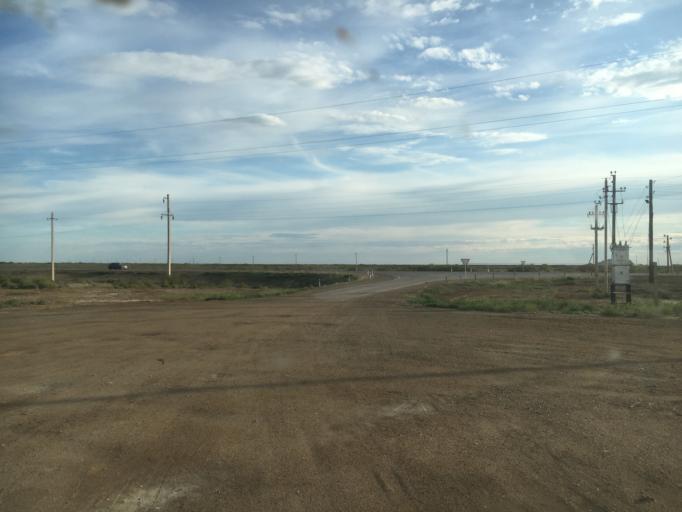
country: KZ
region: Qyzylorda
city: Zhosaly
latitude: 45.2232
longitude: 64.1333
